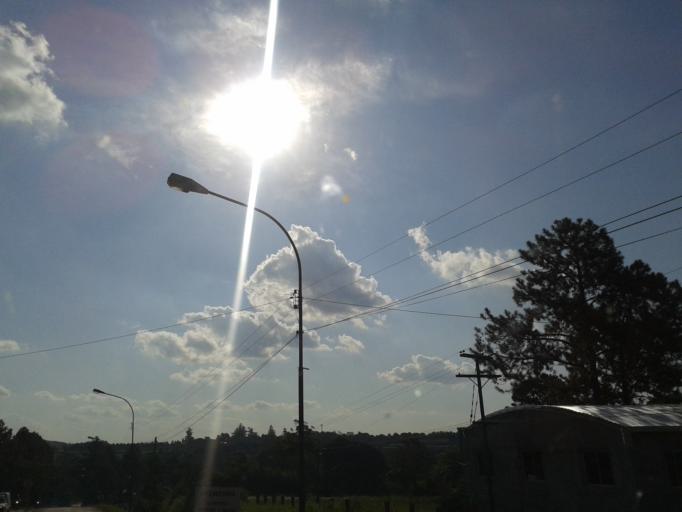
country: AR
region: Misiones
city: Guarani
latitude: -27.4932
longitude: -55.1606
